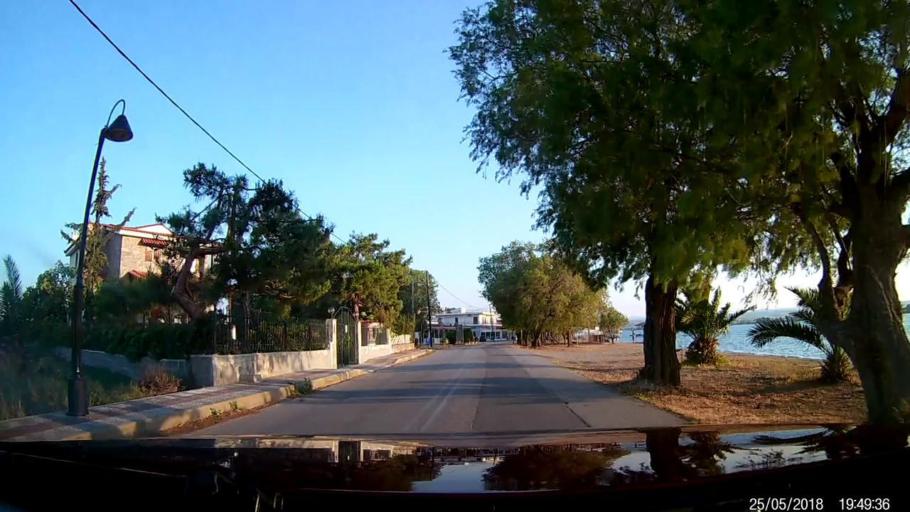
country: GR
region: Central Greece
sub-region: Nomos Evvoias
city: Ayios Nikolaos
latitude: 38.4104
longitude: 23.6409
